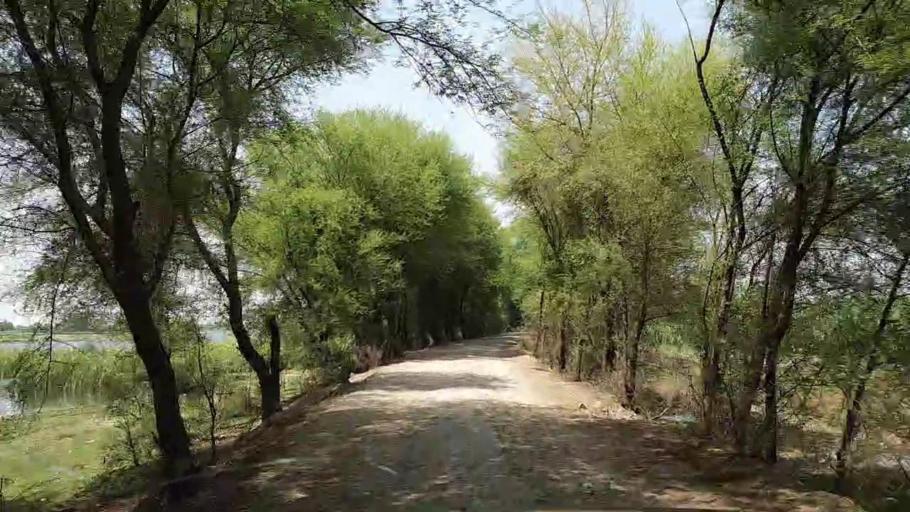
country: PK
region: Sindh
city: Ghotki
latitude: 28.0885
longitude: 69.3109
